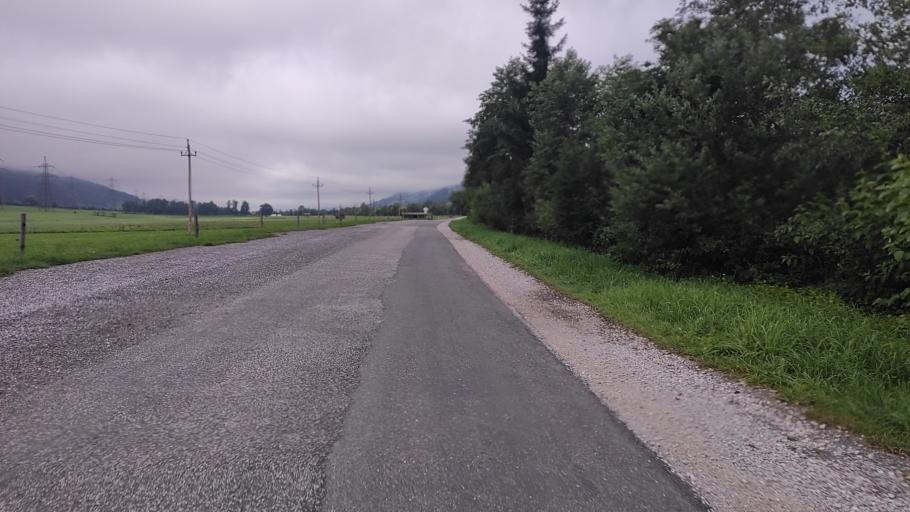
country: AT
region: Salzburg
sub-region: Politischer Bezirk Zell am See
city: Niedernsill
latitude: 47.2806
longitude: 12.6436
